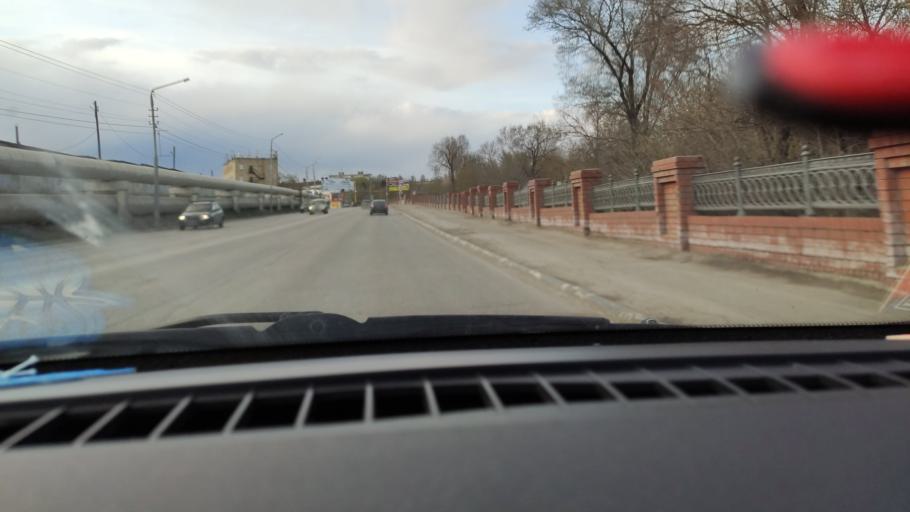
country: RU
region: Saratov
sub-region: Saratovskiy Rayon
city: Saratov
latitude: 51.5649
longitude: 46.0027
